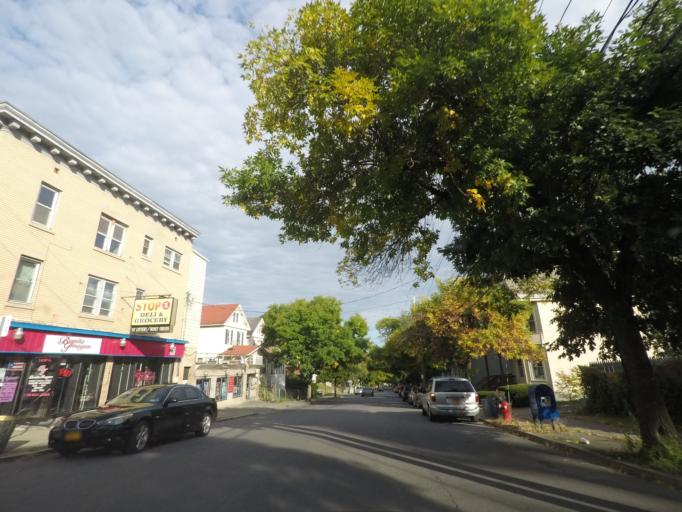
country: US
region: New York
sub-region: Albany County
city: Albany
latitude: 42.6390
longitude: -73.7677
